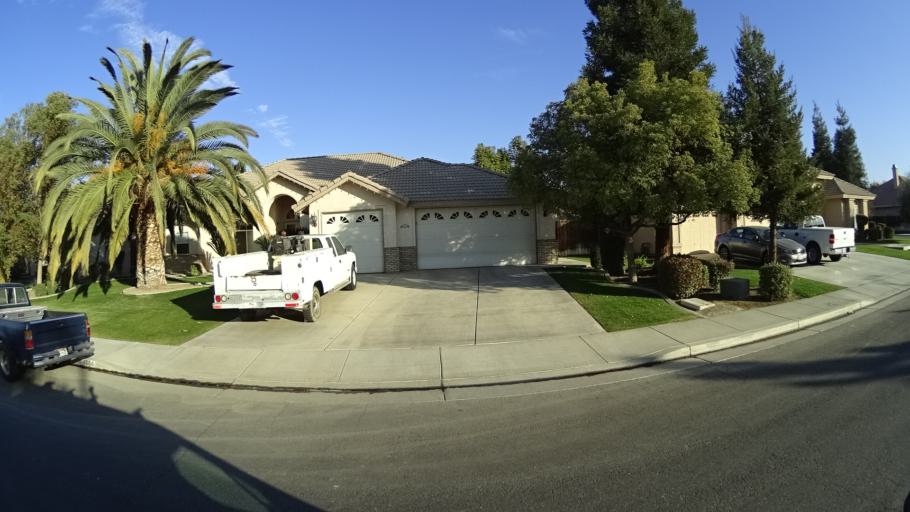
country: US
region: California
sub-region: Kern County
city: Greenfield
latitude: 35.2748
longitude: -119.0535
